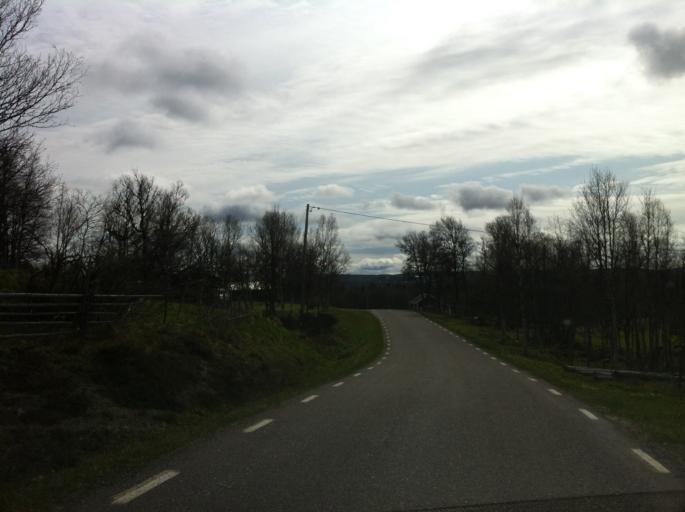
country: NO
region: Hedmark
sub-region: Engerdal
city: Engerdal
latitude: 62.2963
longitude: 12.8074
